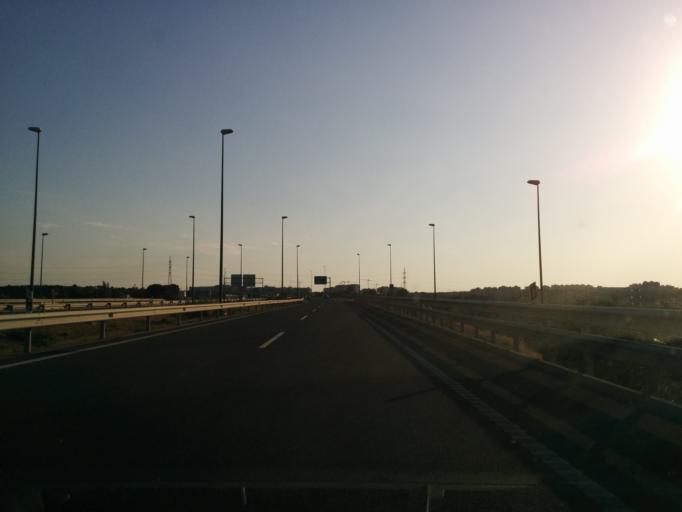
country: ES
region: Aragon
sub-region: Provincia de Zaragoza
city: Zaragoza
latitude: 41.6253
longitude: -0.8501
